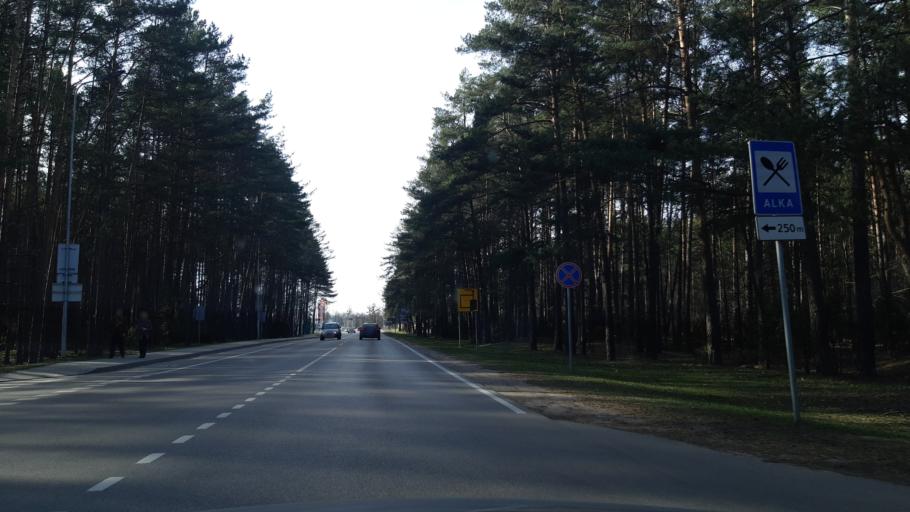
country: LT
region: Alytaus apskritis
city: Druskininkai
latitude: 54.0092
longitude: 23.9969
